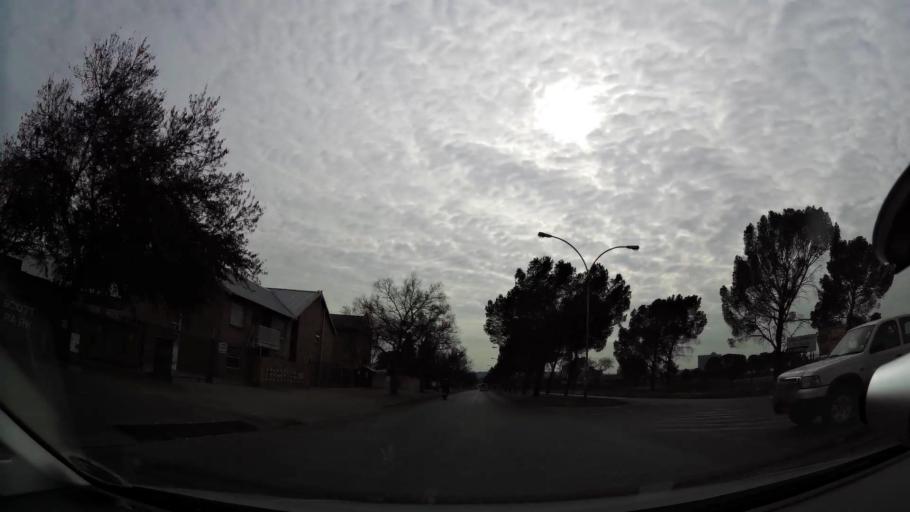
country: ZA
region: Orange Free State
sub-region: Mangaung Metropolitan Municipality
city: Bloemfontein
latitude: -29.1261
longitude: 26.2026
